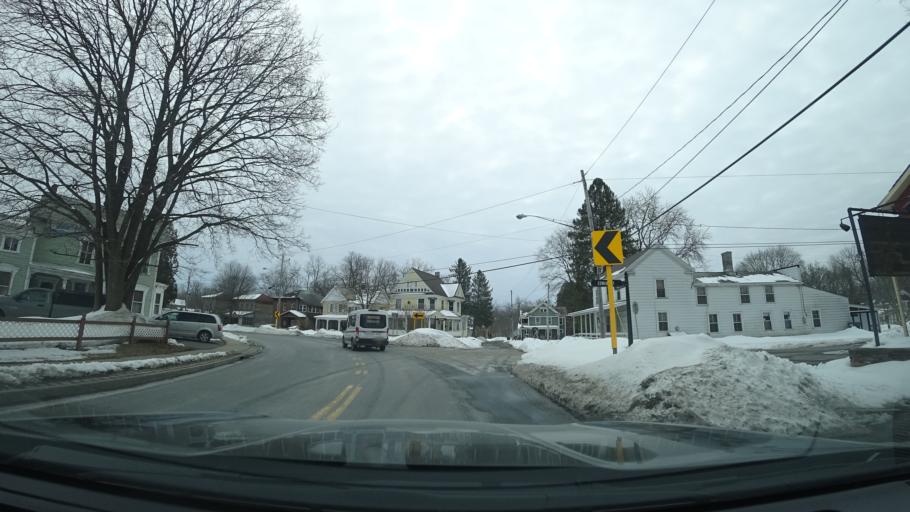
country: US
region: New York
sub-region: Washington County
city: Fort Edward
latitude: 43.2648
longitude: -73.5832
